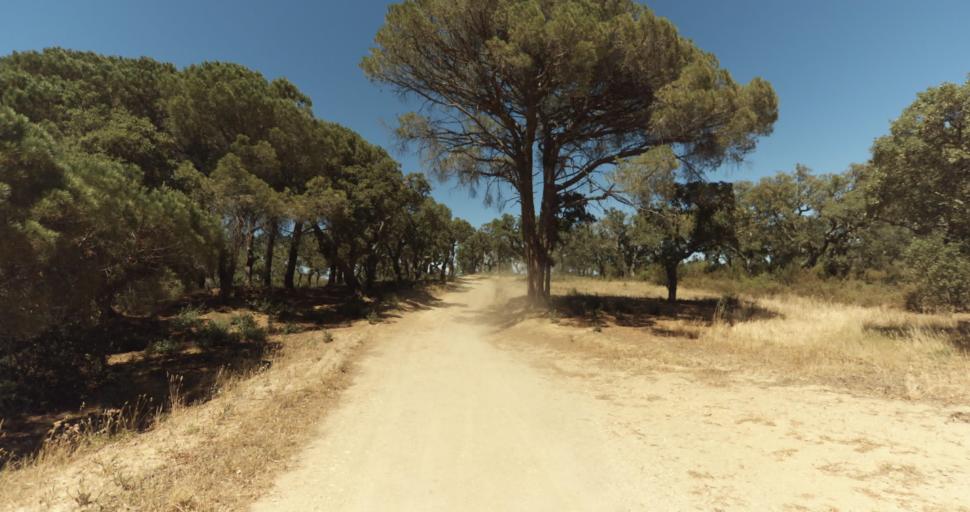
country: FR
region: Provence-Alpes-Cote d'Azur
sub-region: Departement du Var
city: Gassin
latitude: 43.2459
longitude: 6.5613
